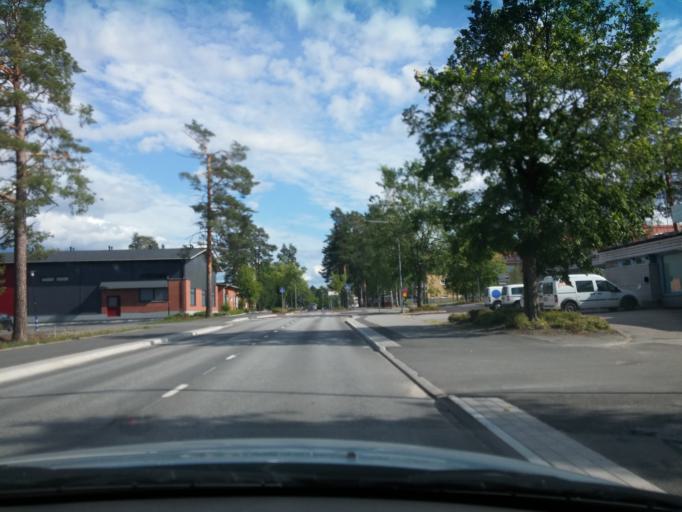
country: FI
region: Central Finland
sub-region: Keuruu
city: Keuruu
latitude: 62.2628
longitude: 24.7034
